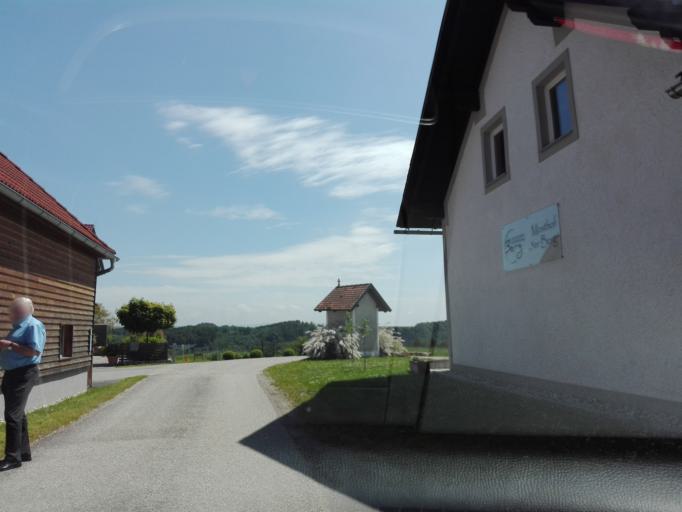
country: AT
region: Upper Austria
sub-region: Politischer Bezirk Rohrbach
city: Atzesberg
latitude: 48.4262
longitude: 13.9123
